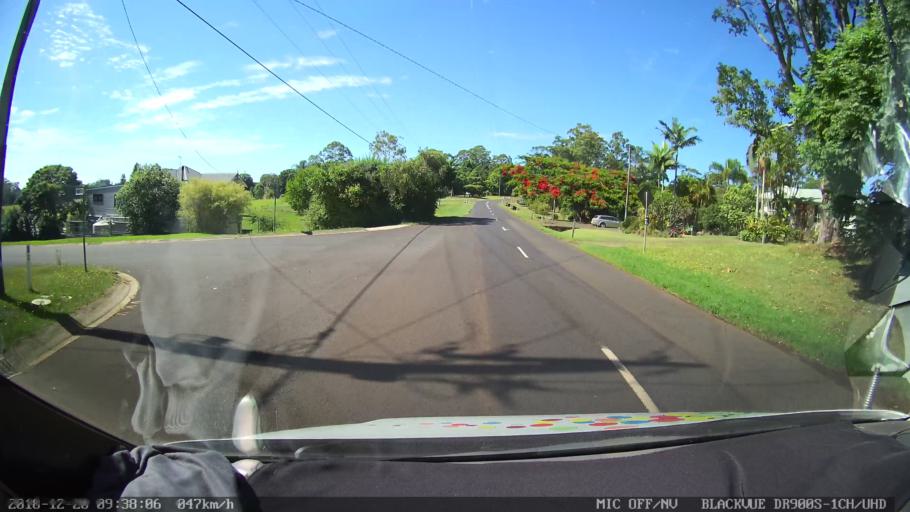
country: AU
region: New South Wales
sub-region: Lismore Municipality
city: Goonellabah
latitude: -28.6883
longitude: 153.3145
